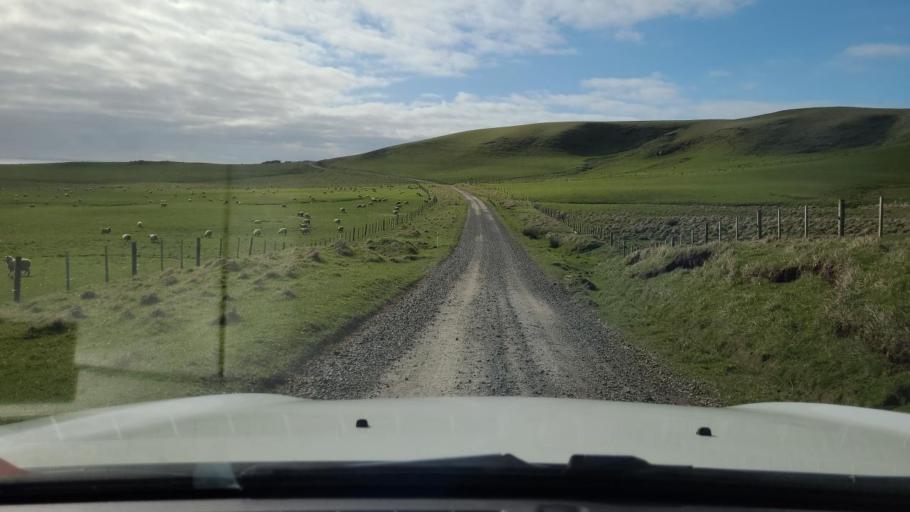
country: NZ
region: Chatham Islands
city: Waitangi
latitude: -44.0266
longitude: -176.6669
